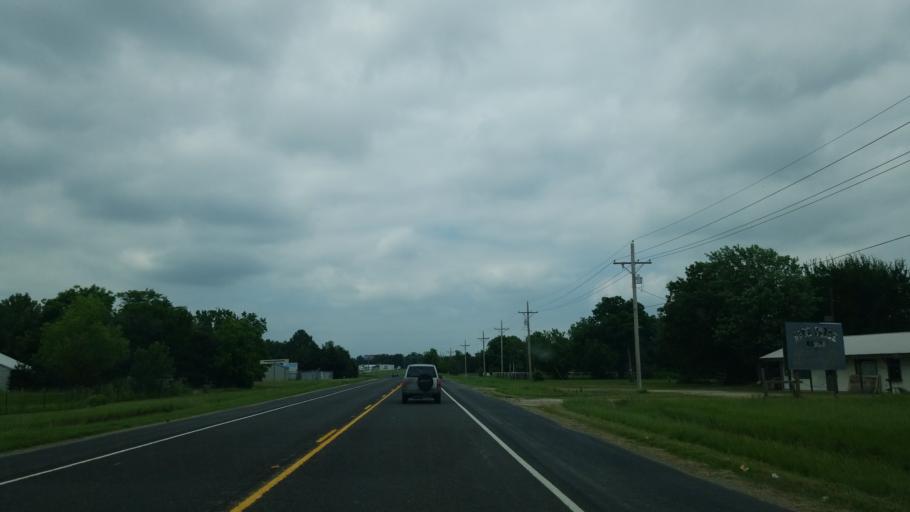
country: US
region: Texas
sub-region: Denton County
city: Pilot Point
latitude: 33.4565
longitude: -96.9204
